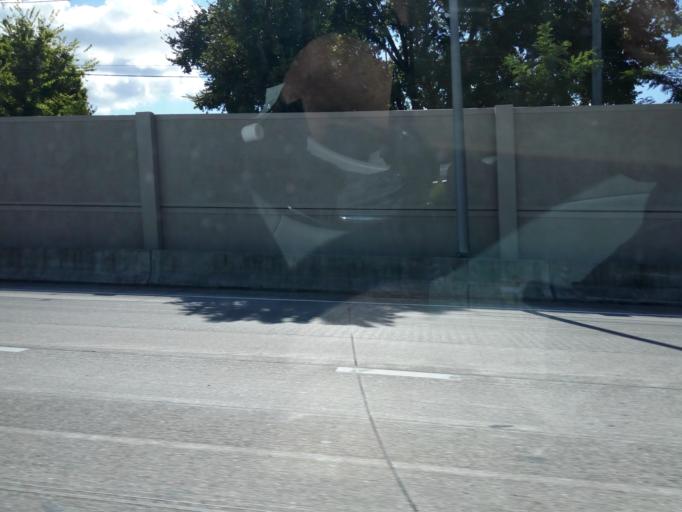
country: US
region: Kentucky
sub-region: Jefferson County
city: Saint Regis Park
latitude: 38.2301
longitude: -85.6327
